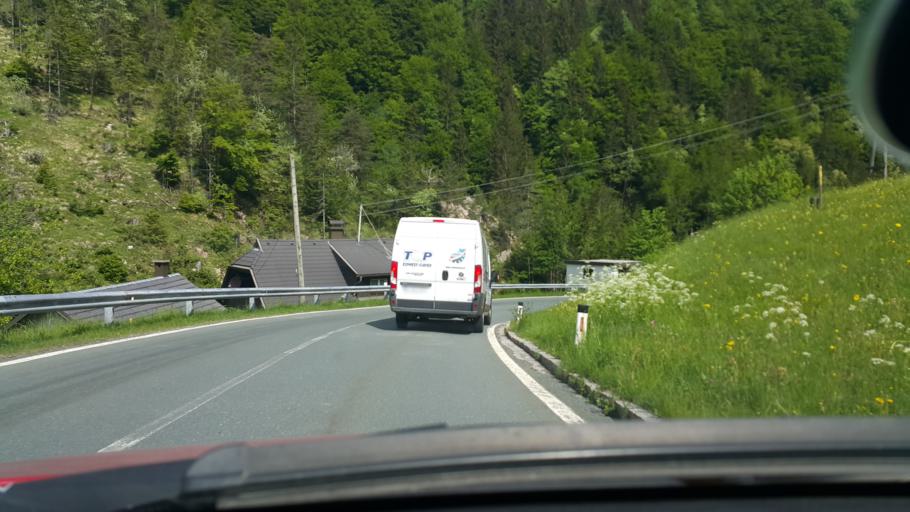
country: AT
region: Carinthia
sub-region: Politischer Bezirk Klagenfurt Land
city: Ferlach
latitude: 46.4543
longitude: 14.2568
